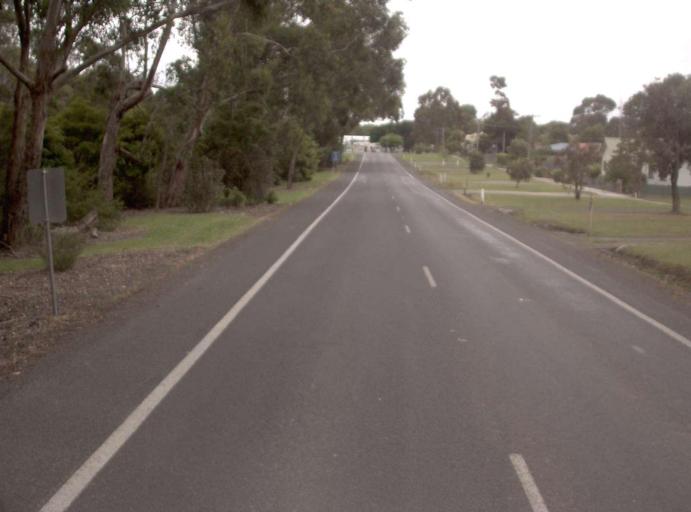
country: AU
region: Victoria
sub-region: Bass Coast
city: North Wonthaggi
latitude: -38.5808
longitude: 146.0089
